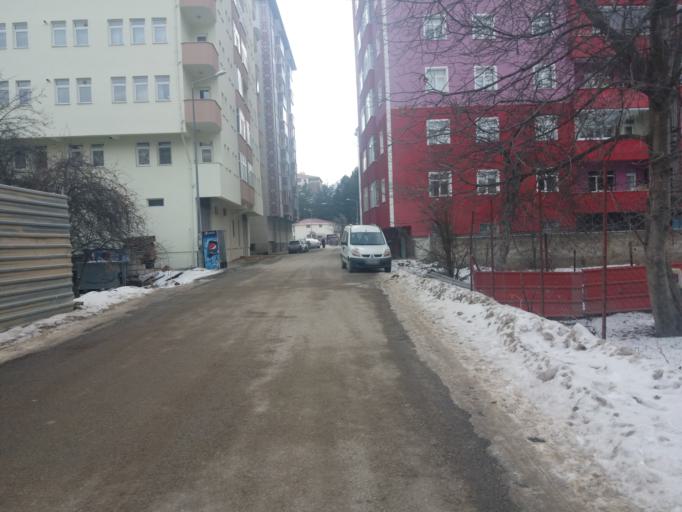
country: TR
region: Gumushane
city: Gumushkhane
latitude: 40.4523
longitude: 39.4929
